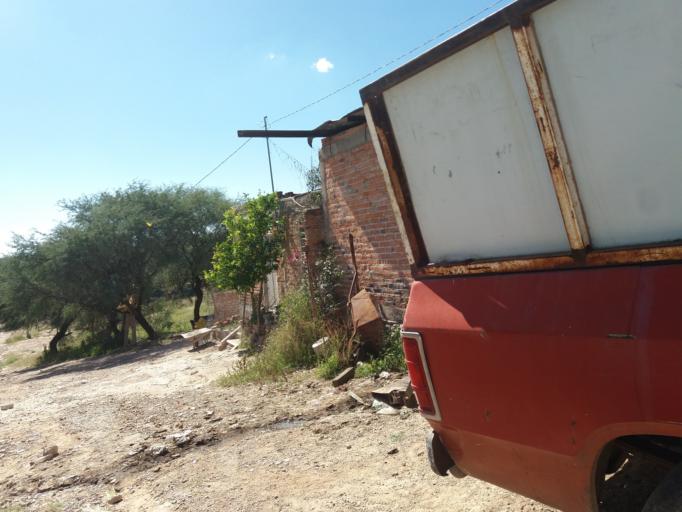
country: MX
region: Aguascalientes
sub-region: Aguascalientes
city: San Sebastian [Fraccionamiento]
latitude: 21.7757
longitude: -102.2281
